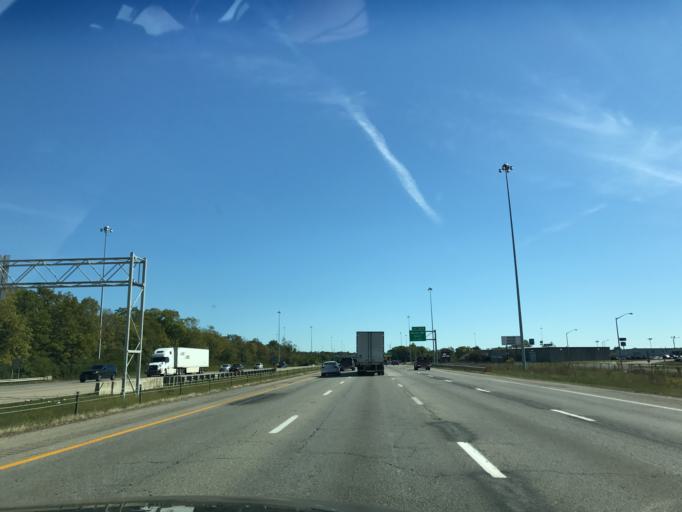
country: US
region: Ohio
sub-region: Franklin County
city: Reynoldsburg
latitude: 39.9331
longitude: -82.8392
